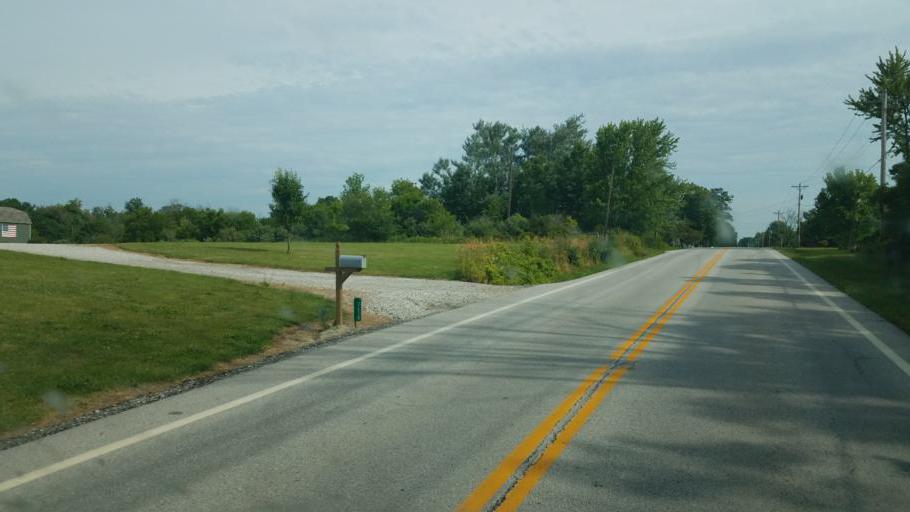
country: US
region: Ohio
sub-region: Medina County
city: Lodi
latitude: 41.0697
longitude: -82.0245
